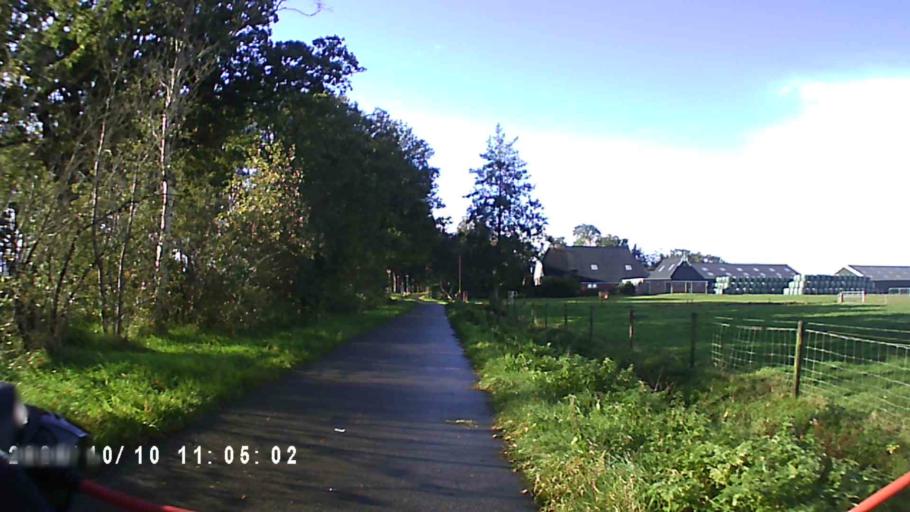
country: NL
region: Friesland
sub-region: Gemeente Achtkarspelen
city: Surhuisterveen
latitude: 53.1299
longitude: 6.2224
